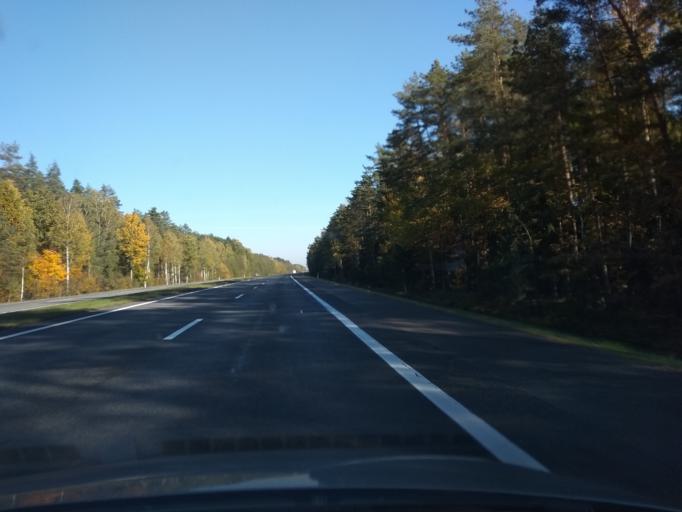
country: BY
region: Brest
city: Nyakhachava
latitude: 52.6488
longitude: 25.2479
